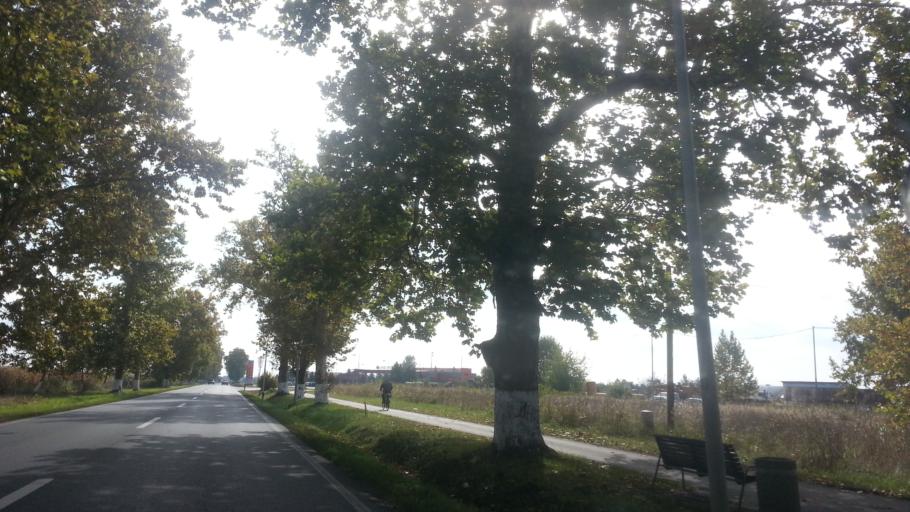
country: RS
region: Autonomna Pokrajina Vojvodina
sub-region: Sremski Okrug
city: Stara Pazova
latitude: 44.9700
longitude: 20.1785
